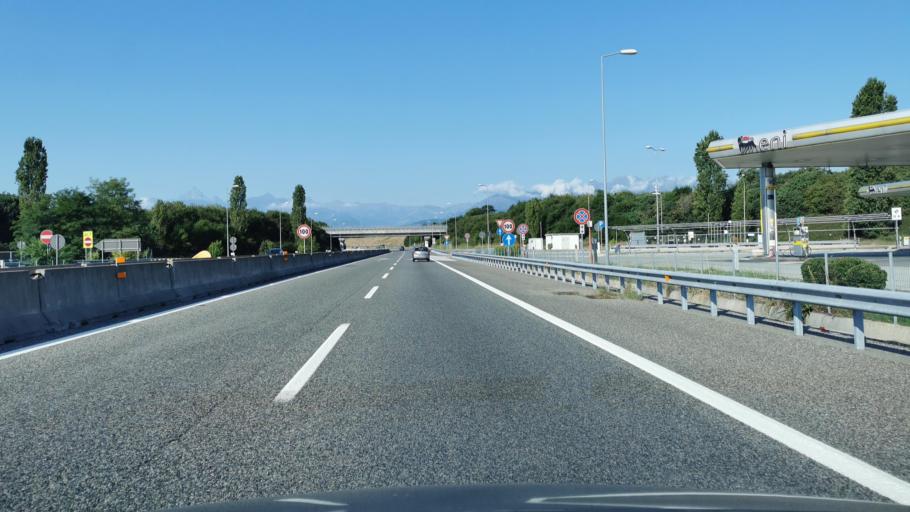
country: IT
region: Piedmont
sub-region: Provincia di Torino
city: Piscina
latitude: 44.9071
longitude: 7.4295
